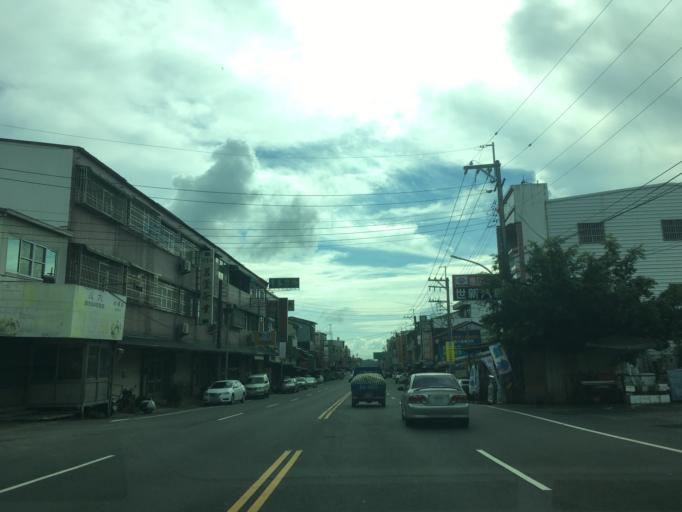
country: TW
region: Taiwan
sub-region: Chiayi
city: Jiayi Shi
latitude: 23.4415
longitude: 120.5302
